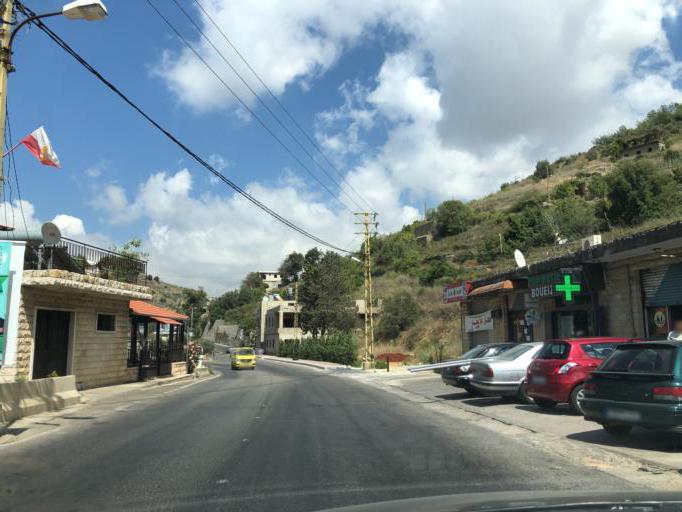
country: LB
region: Mont-Liban
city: Beit ed Dine
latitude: 33.6987
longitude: 35.5965
